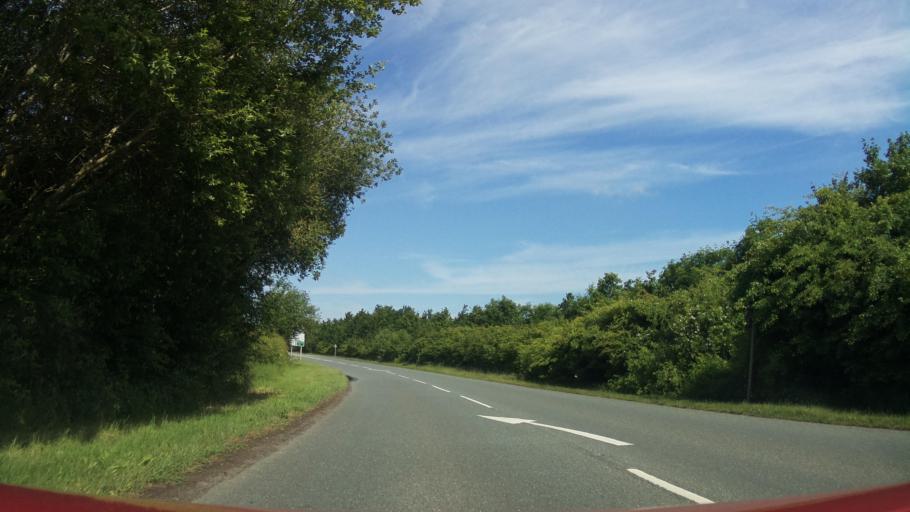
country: GB
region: England
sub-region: Lincolnshire
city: Skellingthorpe
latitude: 53.1651
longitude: -0.6394
